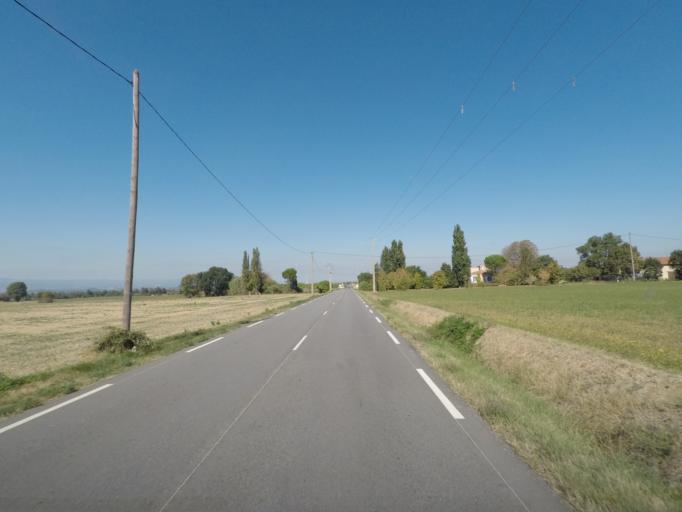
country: FR
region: Rhone-Alpes
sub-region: Departement de la Drome
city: Upie
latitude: 44.7979
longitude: 5.0176
